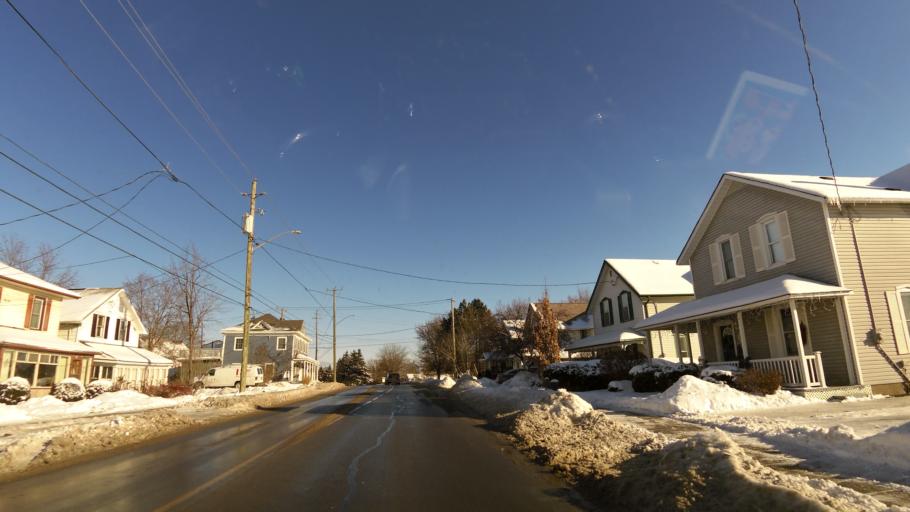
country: CA
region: Ontario
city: Quinte West
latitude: 44.3064
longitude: -77.8021
